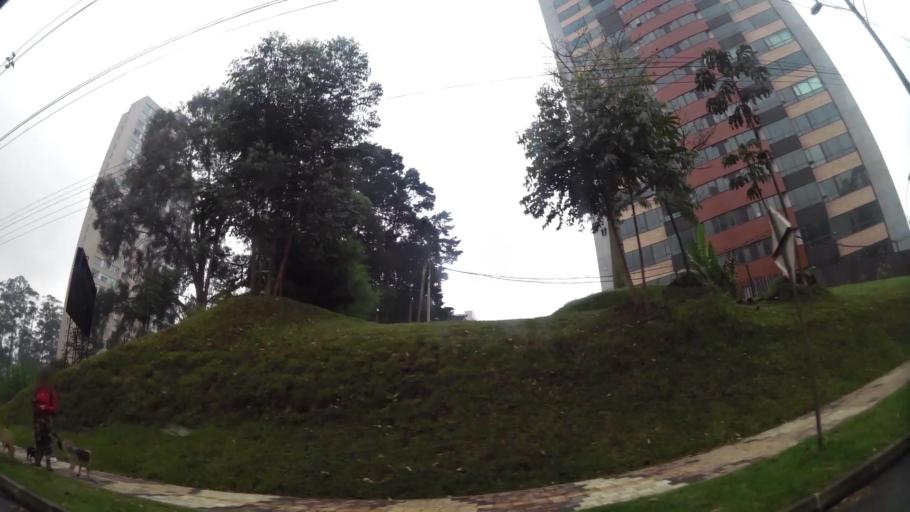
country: CO
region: Antioquia
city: Envigado
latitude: 6.1834
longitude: -75.5587
